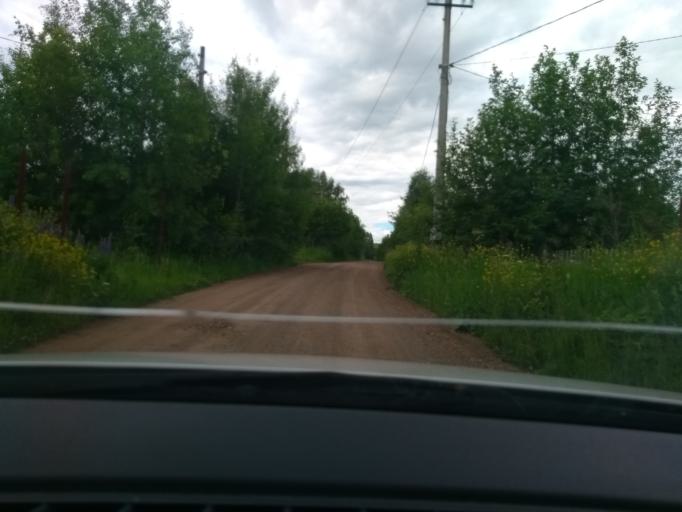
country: RU
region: Perm
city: Sylva
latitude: 57.8440
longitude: 56.7971
